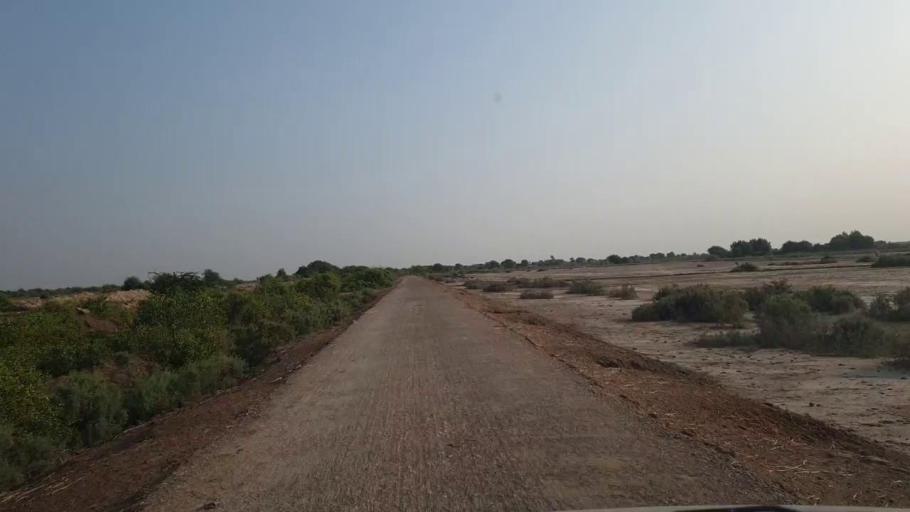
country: PK
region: Sindh
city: Rajo Khanani
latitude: 25.0089
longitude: 68.7860
